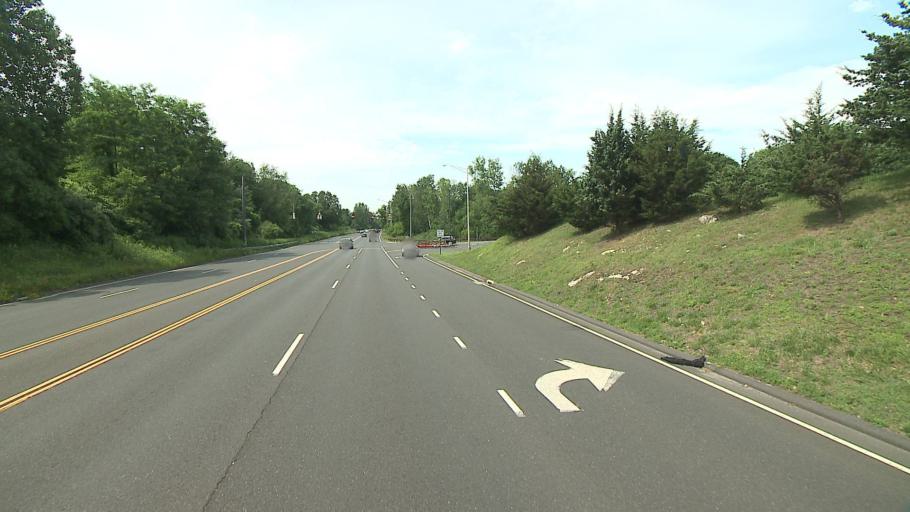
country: US
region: Connecticut
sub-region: Fairfield County
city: Danbury
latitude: 41.4264
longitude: -73.4125
